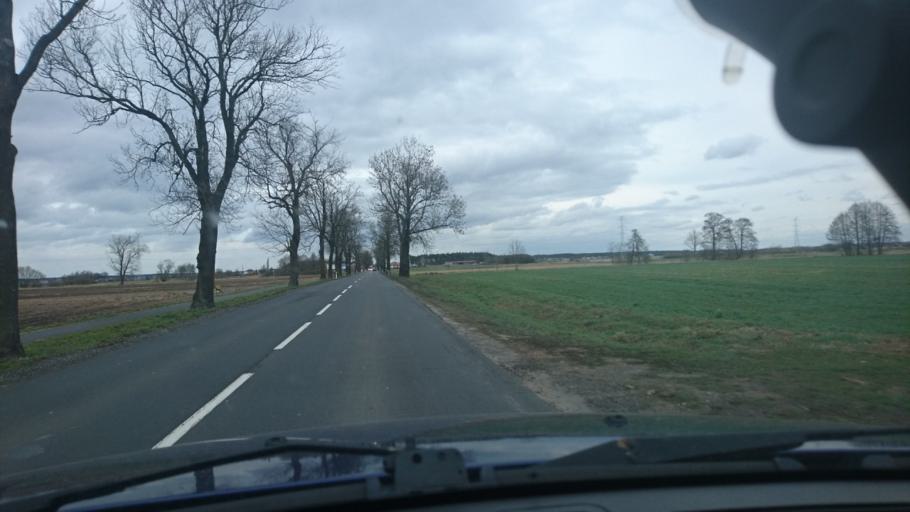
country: PL
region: Greater Poland Voivodeship
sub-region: Powiat ostrowski
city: Odolanow
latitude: 51.5771
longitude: 17.6983
